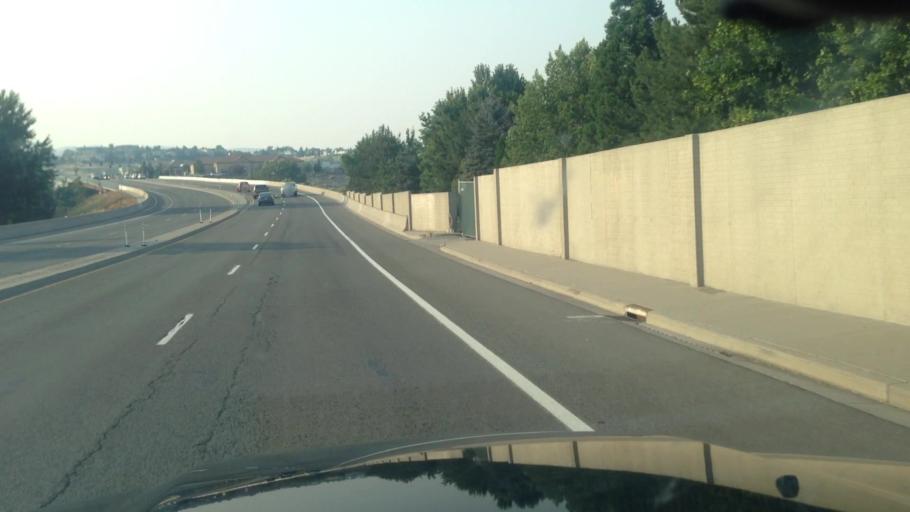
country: US
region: Nevada
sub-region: Washoe County
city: Reno
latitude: 39.5092
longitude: -119.8586
